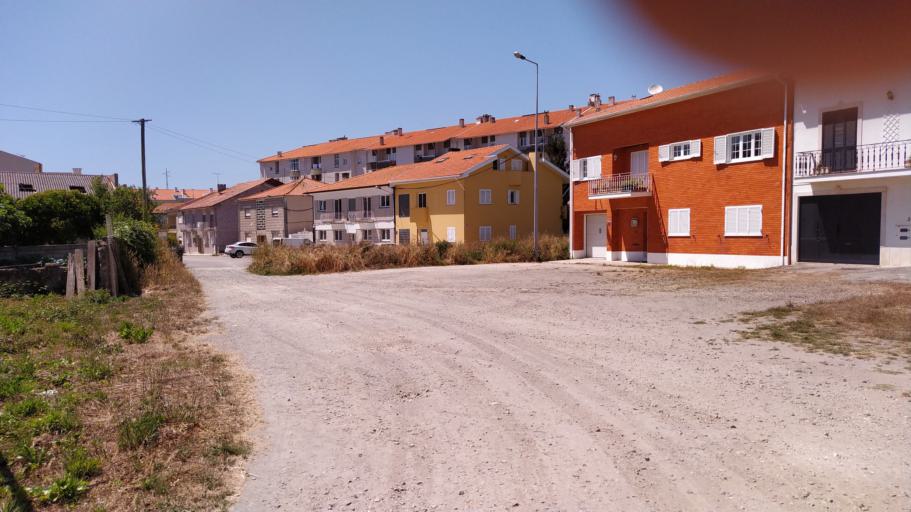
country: PT
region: Aveiro
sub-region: Aveiro
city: Aveiro
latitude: 40.6475
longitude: -8.6352
